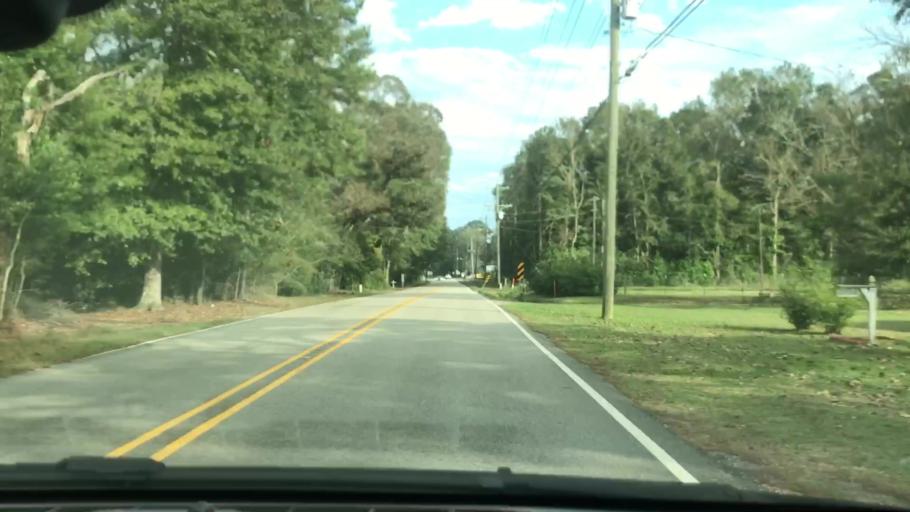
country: US
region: Louisiana
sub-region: Saint Tammany Parish
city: Abita Springs
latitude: 30.5325
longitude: -89.8786
